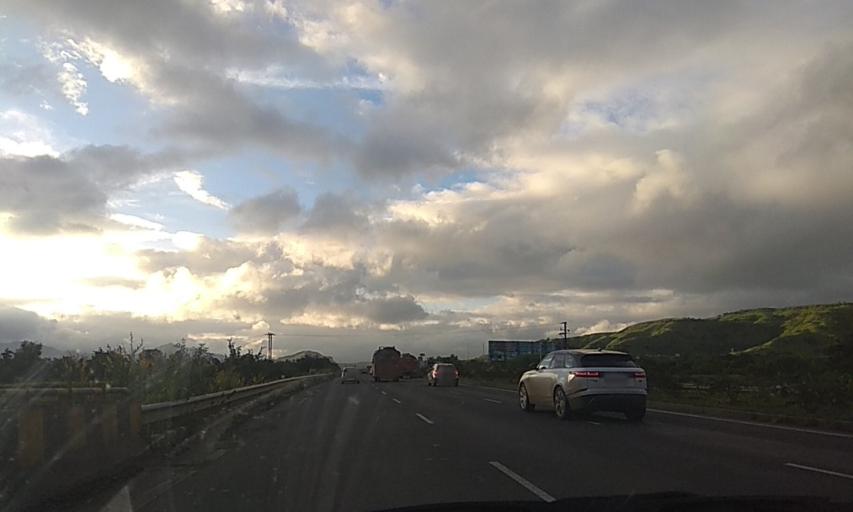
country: IN
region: Maharashtra
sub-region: Satara Division
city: Satara
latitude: 17.7338
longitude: 74.0136
